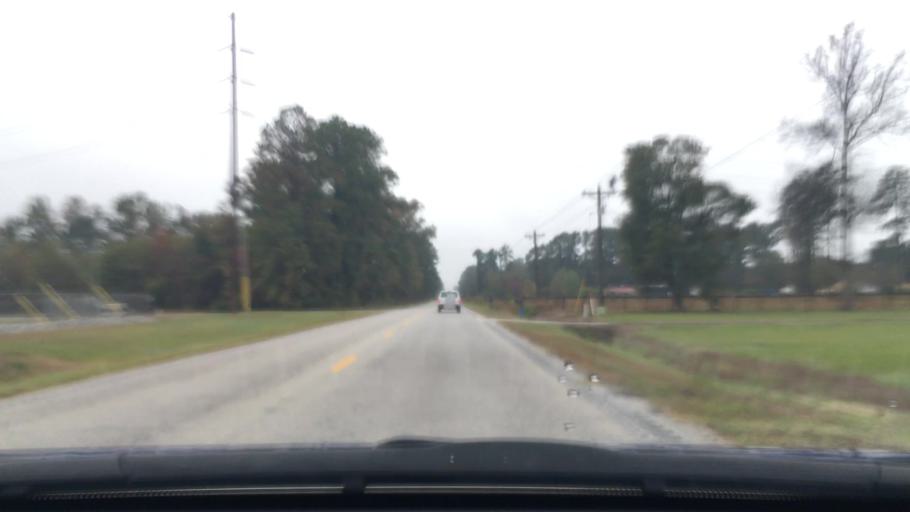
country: US
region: South Carolina
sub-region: Darlington County
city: Darlington
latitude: 34.2695
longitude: -79.9252
